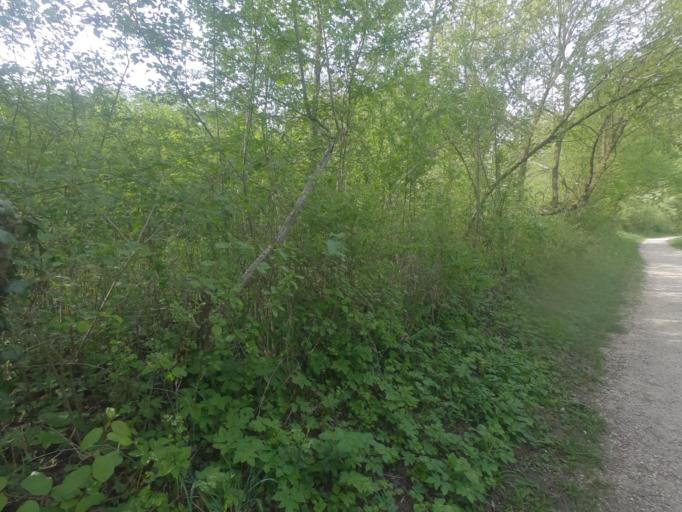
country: CH
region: Bern
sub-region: Oberaargau
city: Attiswil
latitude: 47.2341
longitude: 7.6275
